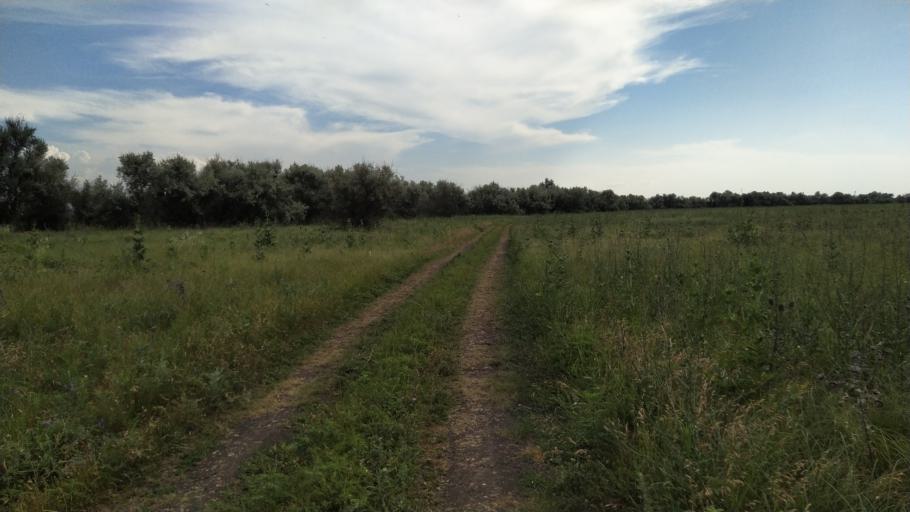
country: RU
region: Rostov
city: Kuleshovka
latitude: 47.1247
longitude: 39.6271
